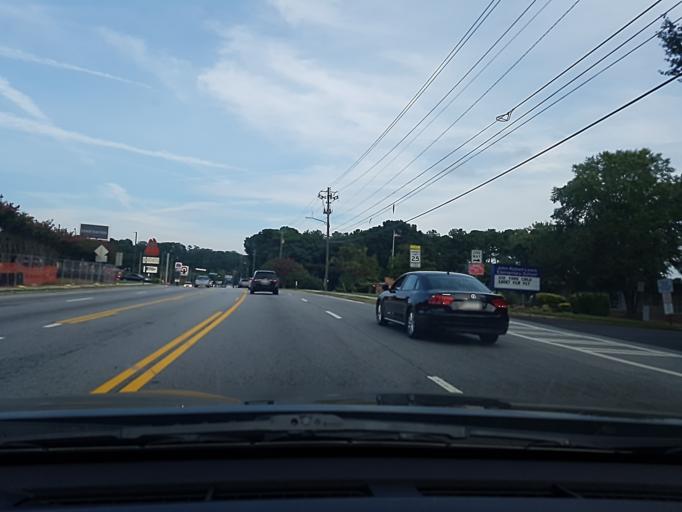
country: US
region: Georgia
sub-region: DeKalb County
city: North Druid Hills
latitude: 33.8273
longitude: -84.3289
